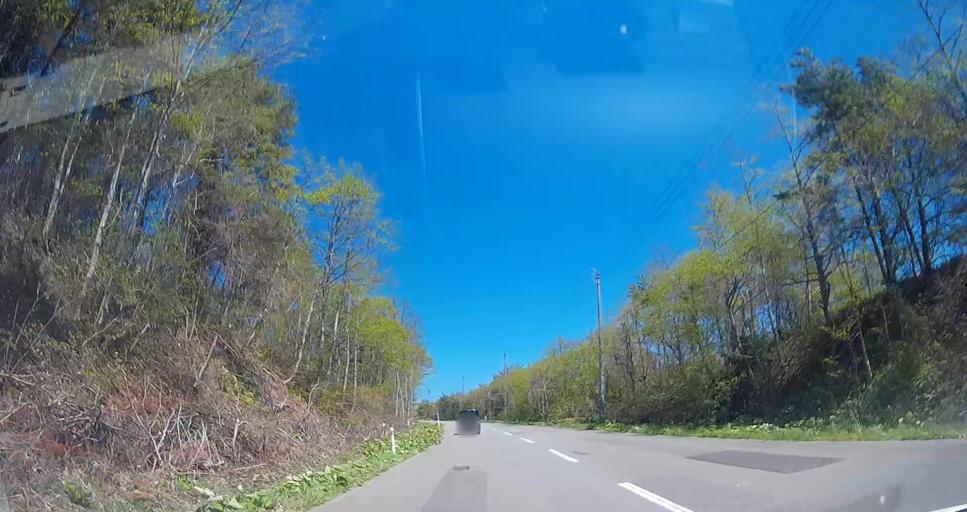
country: JP
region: Aomori
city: Mutsu
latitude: 41.2789
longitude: 141.3940
